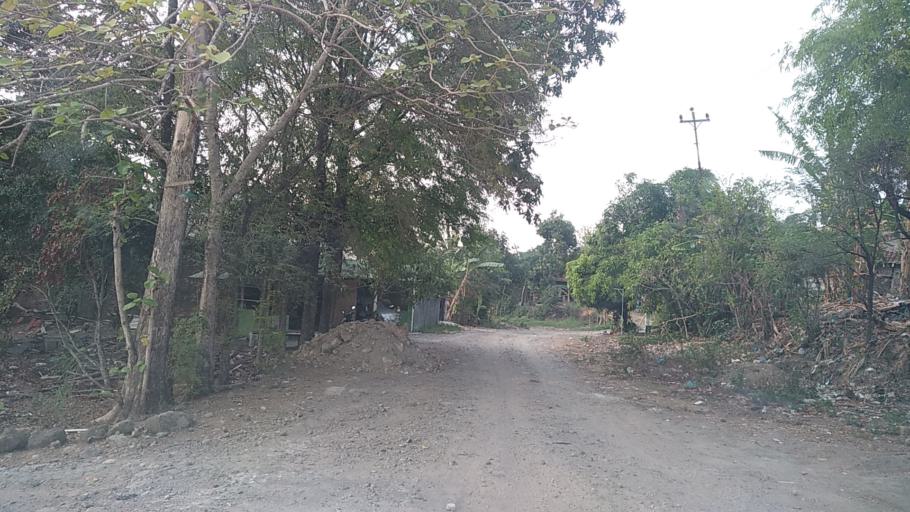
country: ID
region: Central Java
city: Mranggen
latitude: -7.0662
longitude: 110.4820
